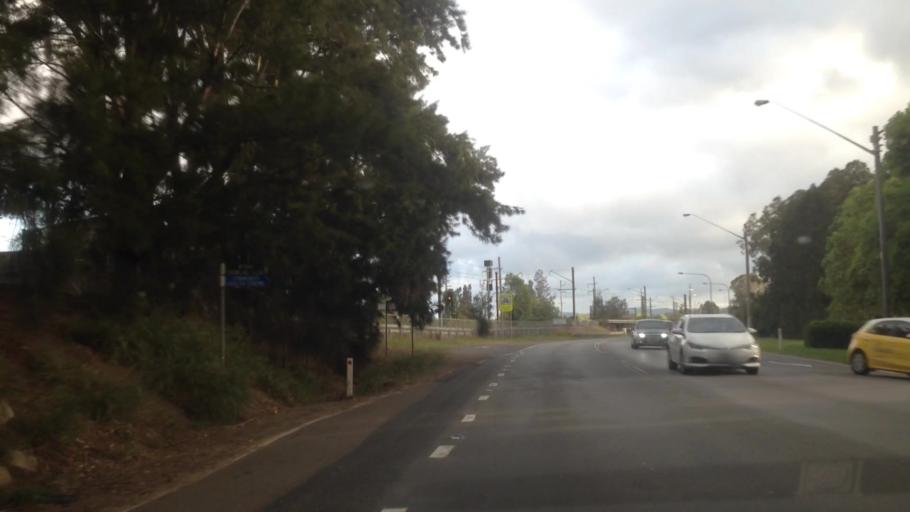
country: AU
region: New South Wales
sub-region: Wyong Shire
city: Chittaway Bay
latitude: -33.2891
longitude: 151.4241
